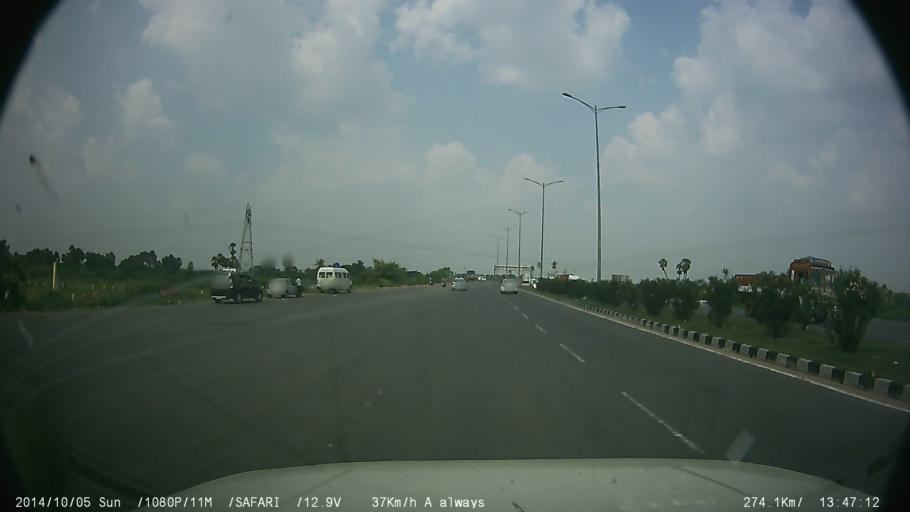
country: IN
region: Tamil Nadu
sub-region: Villupuram
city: Vikravandi
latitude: 12.0249
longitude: 79.5383
